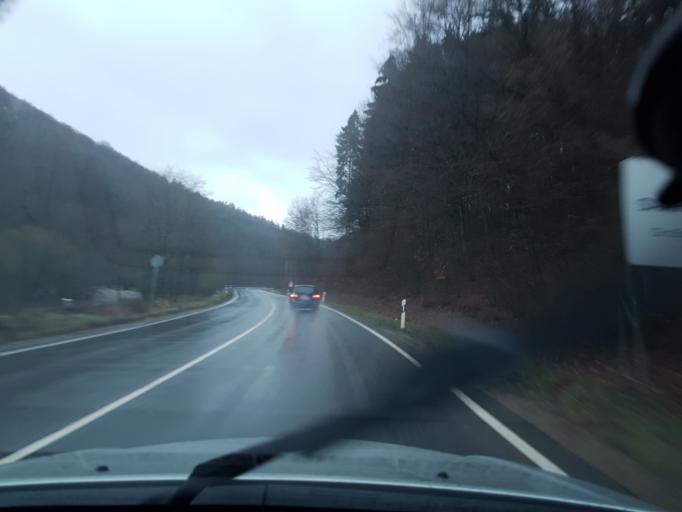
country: DE
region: Saarland
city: Nohfelden
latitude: 49.5997
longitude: 7.1435
